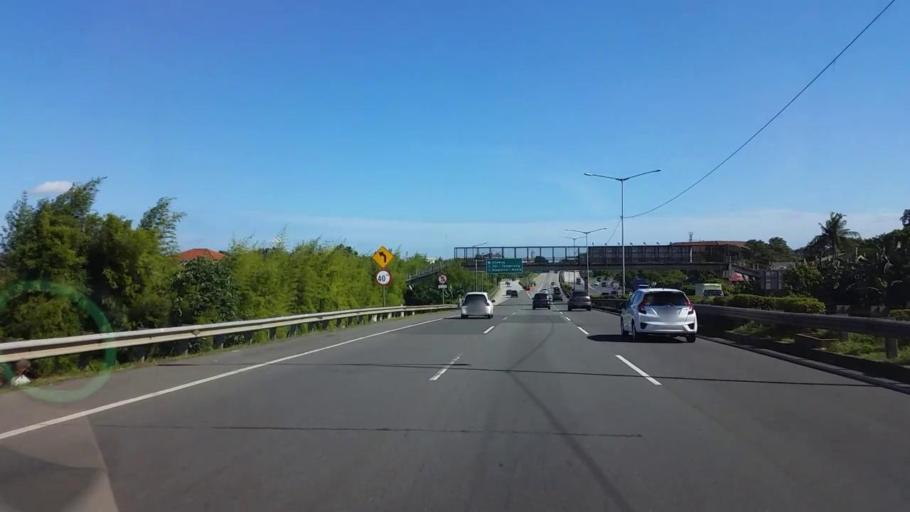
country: ID
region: Banten
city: South Tangerang
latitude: -6.2553
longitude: 106.7608
